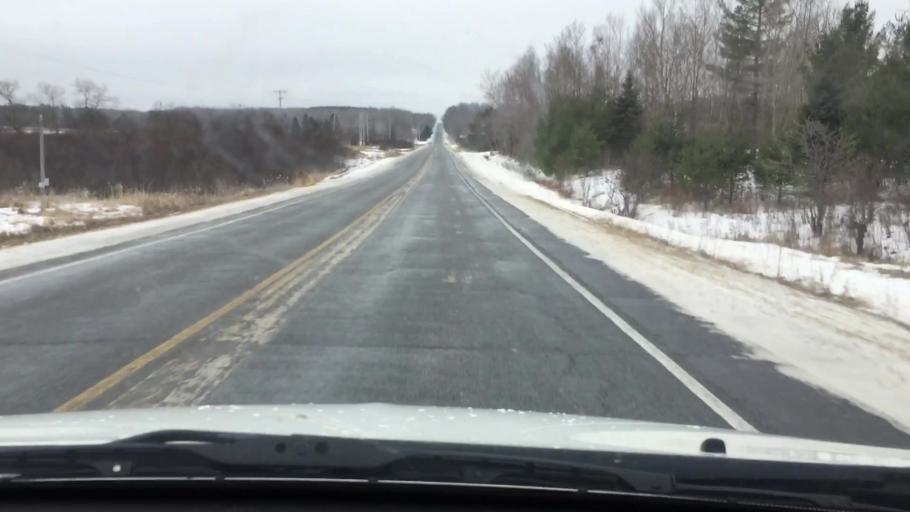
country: US
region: Michigan
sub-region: Wexford County
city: Cadillac
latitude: 44.1075
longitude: -85.4442
